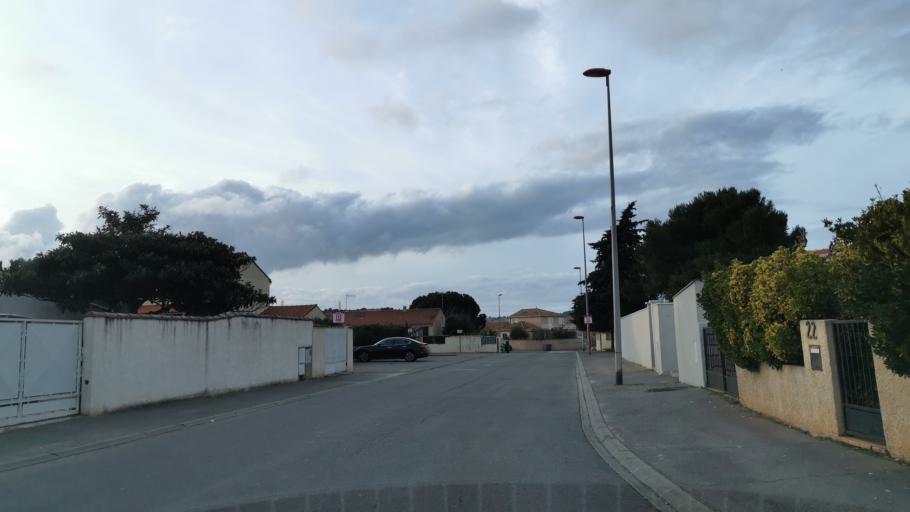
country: FR
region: Languedoc-Roussillon
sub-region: Departement de l'Aude
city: Narbonne
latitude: 43.1876
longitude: 2.9796
